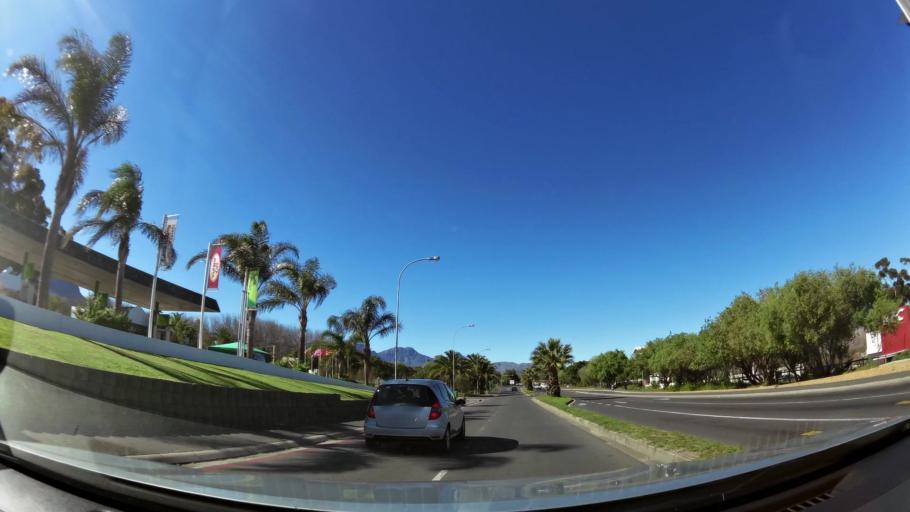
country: ZA
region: Western Cape
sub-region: Cape Winelands District Municipality
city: Stellenbosch
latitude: -34.0683
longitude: 18.8227
